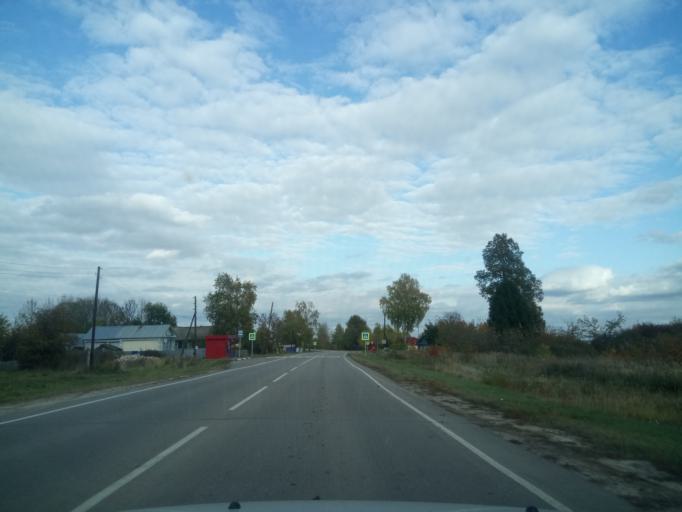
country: RU
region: Nizjnij Novgorod
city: Bol'shoye Boldino
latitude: 54.9318
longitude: 45.1795
